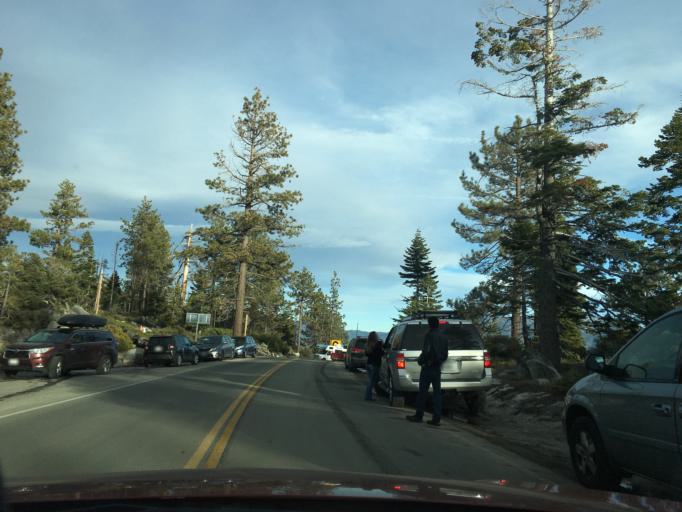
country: US
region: California
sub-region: El Dorado County
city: South Lake Tahoe
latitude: 38.9514
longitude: -120.0854
